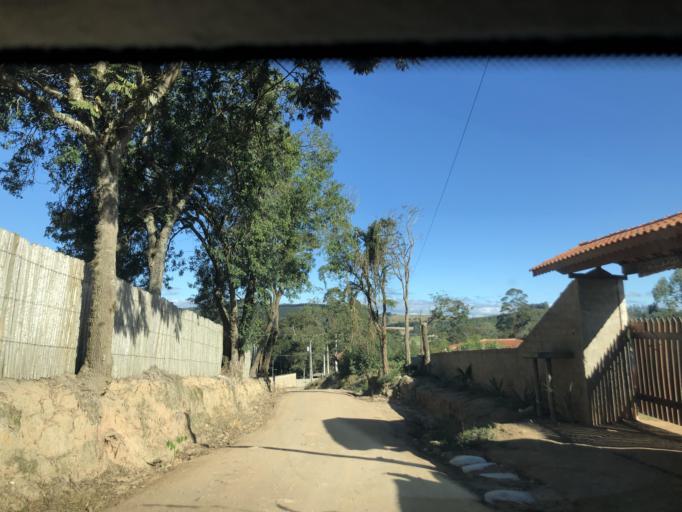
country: BR
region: Sao Paulo
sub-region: Pilar Do Sul
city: Pilar do Sul
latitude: -23.8166
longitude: -47.6311
